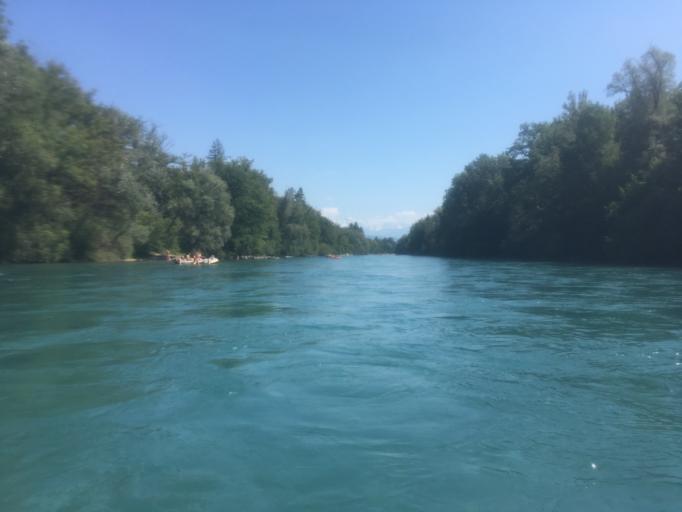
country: CH
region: Bern
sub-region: Bern-Mittelland District
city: Rubigen
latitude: 46.8995
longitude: 7.5280
